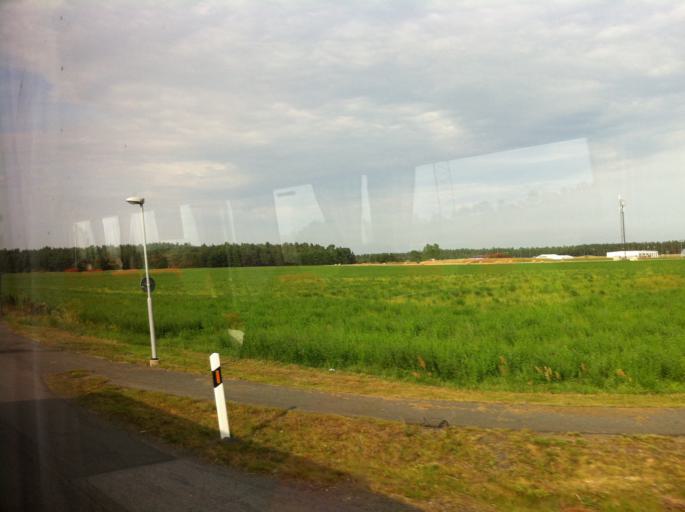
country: SE
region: Skane
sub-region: Kristianstads Kommun
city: Degeberga
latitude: 55.9237
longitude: 14.0741
